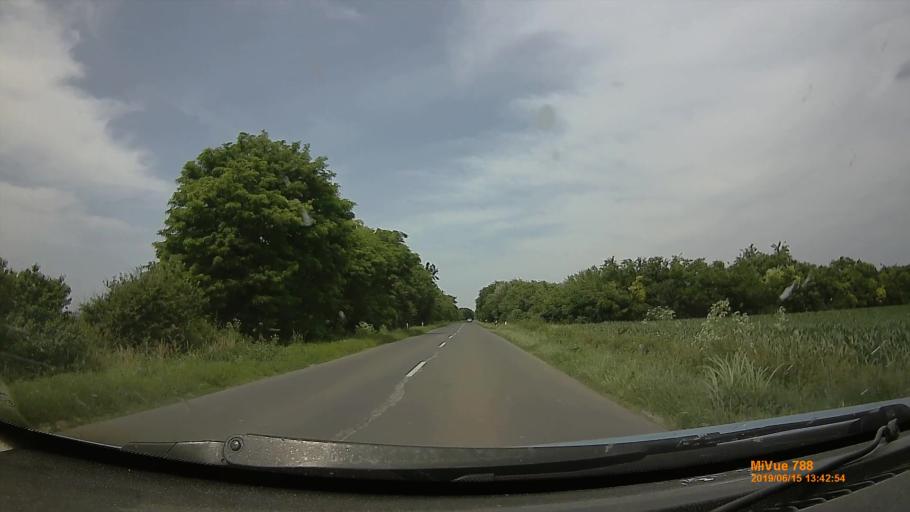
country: HU
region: Tolna
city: Iregszemcse
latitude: 46.6701
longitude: 18.1828
